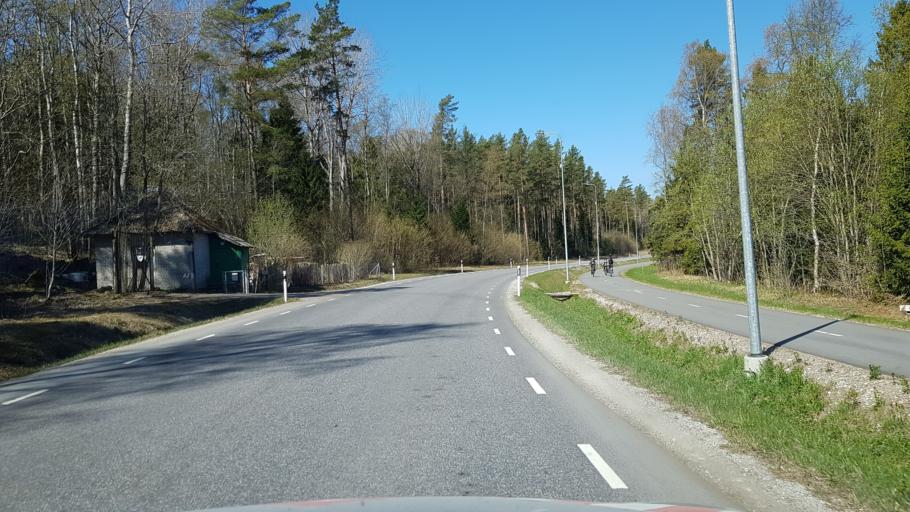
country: EE
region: Harju
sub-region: Viimsi vald
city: Viimsi
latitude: 59.5235
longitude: 24.8878
